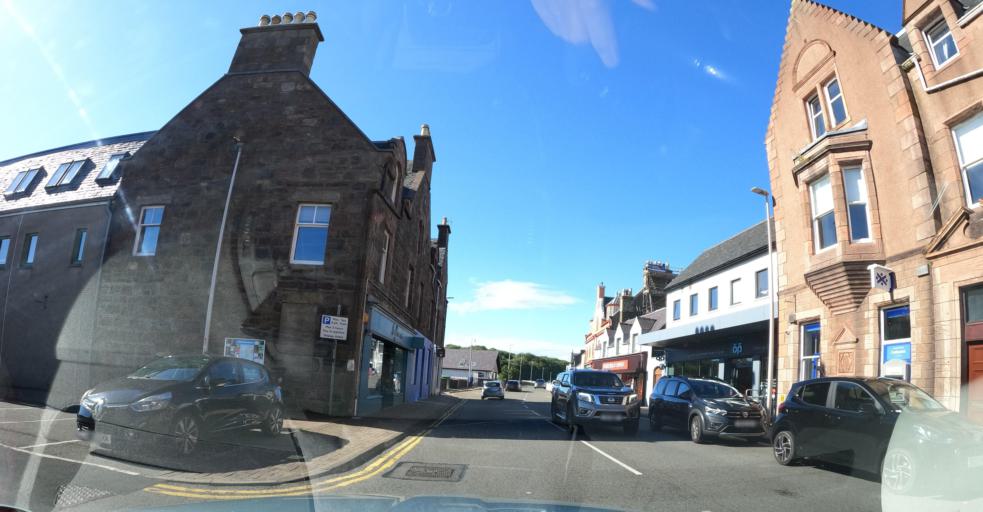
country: GB
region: Scotland
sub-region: Eilean Siar
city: Stornoway
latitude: 58.2093
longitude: -6.3885
